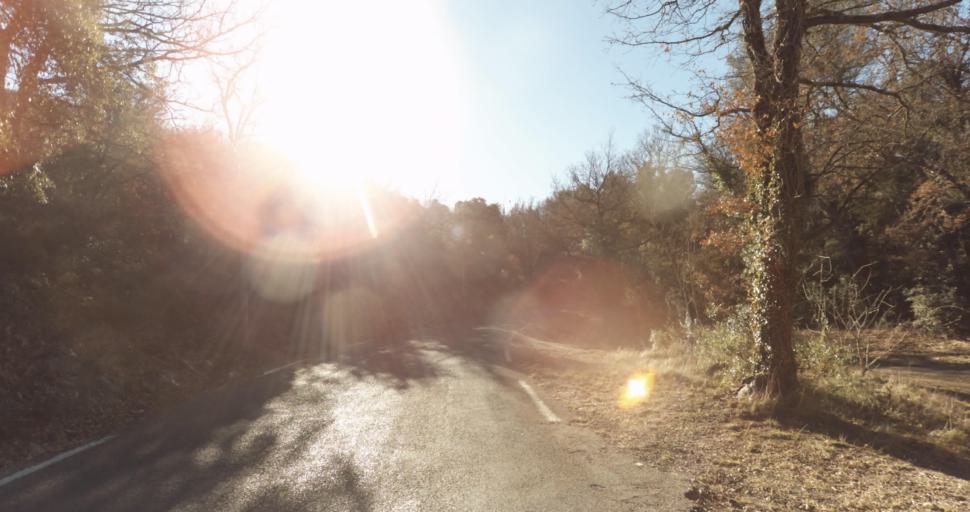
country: FR
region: Provence-Alpes-Cote d'Azur
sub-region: Departement des Bouches-du-Rhone
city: Peypin
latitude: 43.3709
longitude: 5.5642
